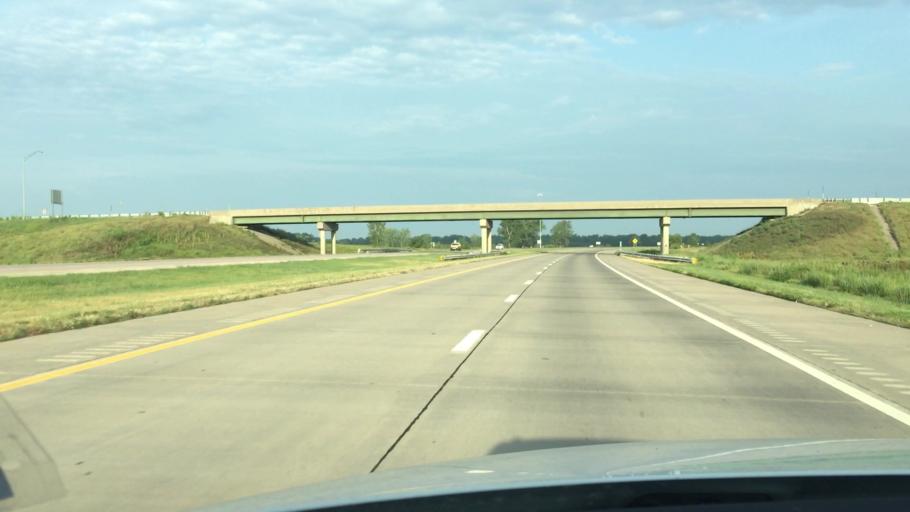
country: US
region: Kansas
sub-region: Doniphan County
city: Elwood
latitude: 39.7414
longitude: -94.8924
